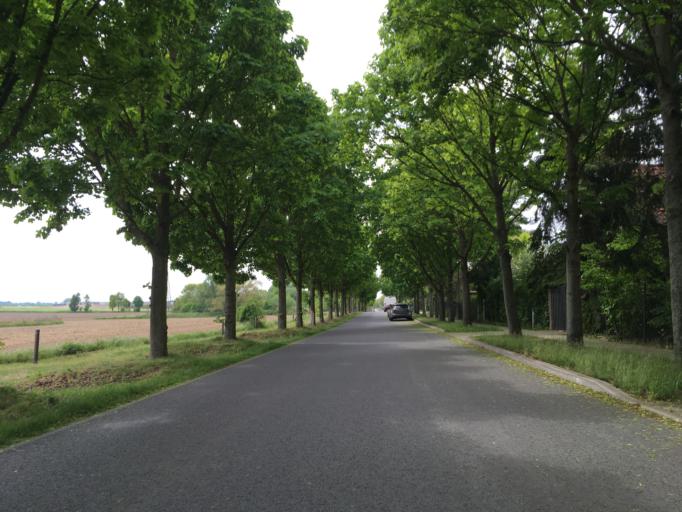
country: DE
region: Berlin
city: Buch
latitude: 52.6235
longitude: 13.5188
